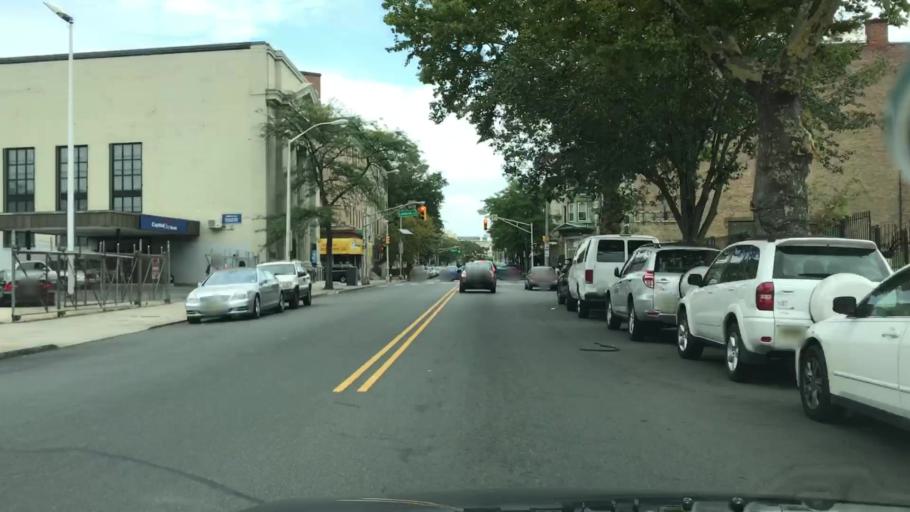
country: US
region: New Jersey
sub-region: Hudson County
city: Bayonne
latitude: 40.6936
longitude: -74.0931
